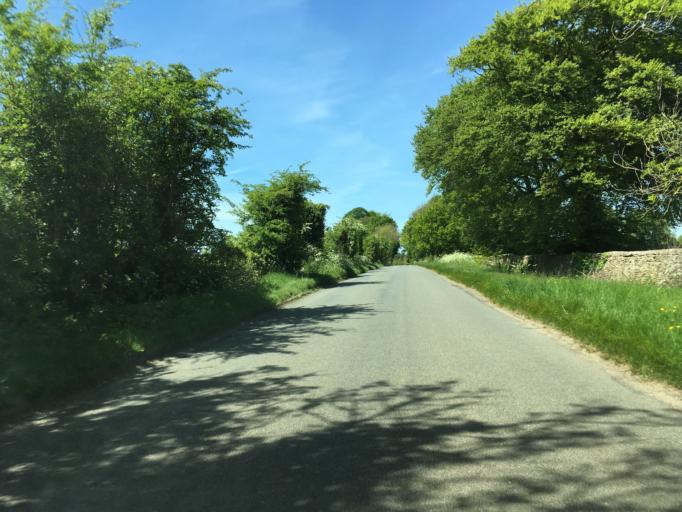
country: GB
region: England
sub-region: Gloucestershire
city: Coates
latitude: 51.7032
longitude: -2.0304
